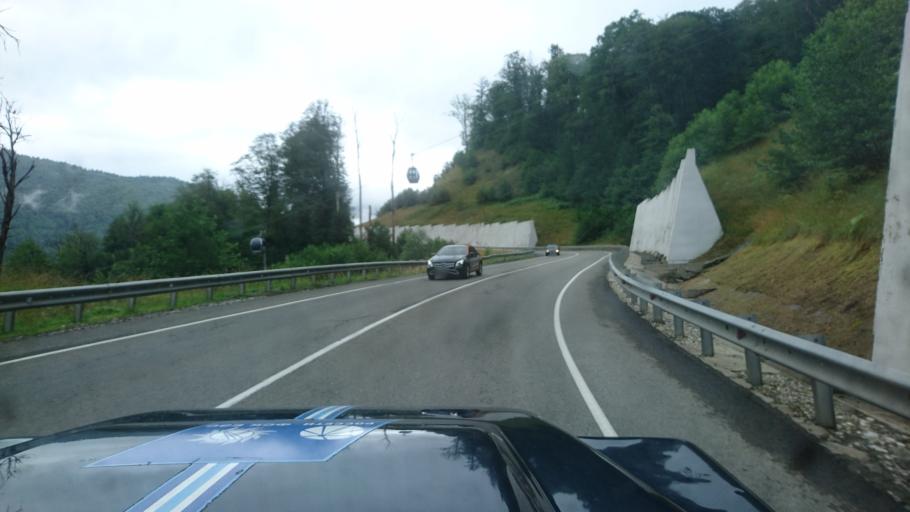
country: RU
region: Krasnodarskiy
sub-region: Sochi City
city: Krasnaya Polyana
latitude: 43.6673
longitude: 40.2967
